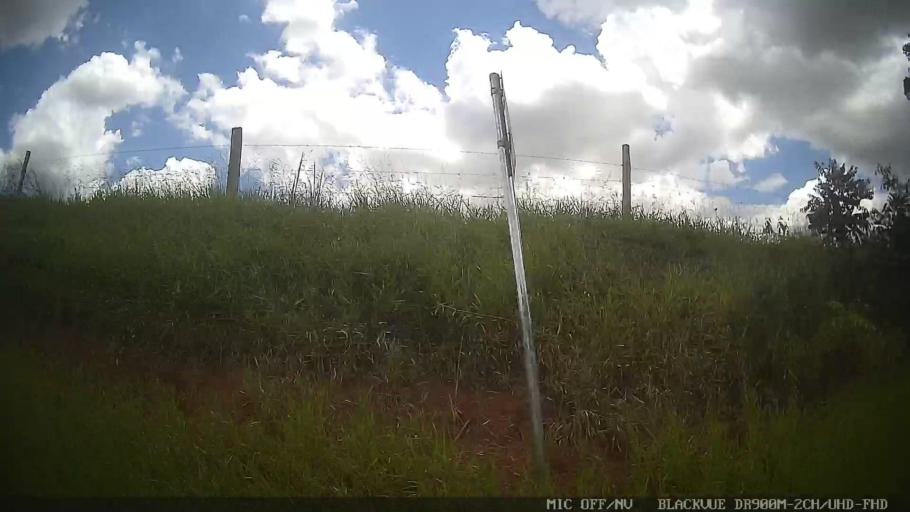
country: BR
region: Sao Paulo
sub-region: Braganca Paulista
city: Braganca Paulista
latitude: -23.0127
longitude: -46.4919
